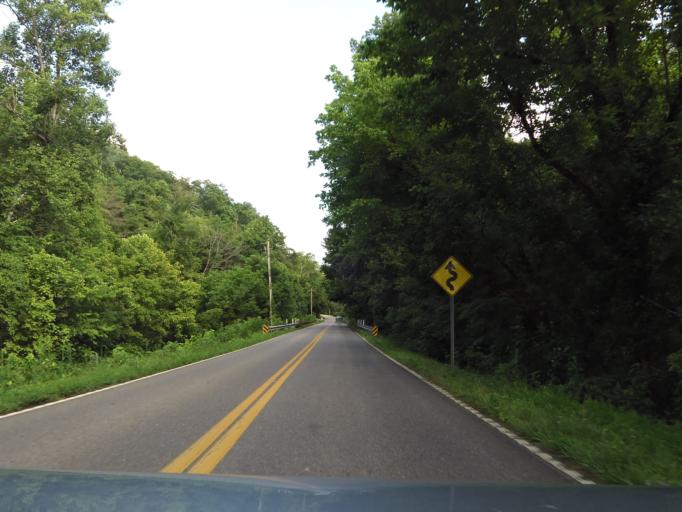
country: US
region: Tennessee
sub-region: Loudon County
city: Greenback
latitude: 35.6082
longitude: -84.0886
